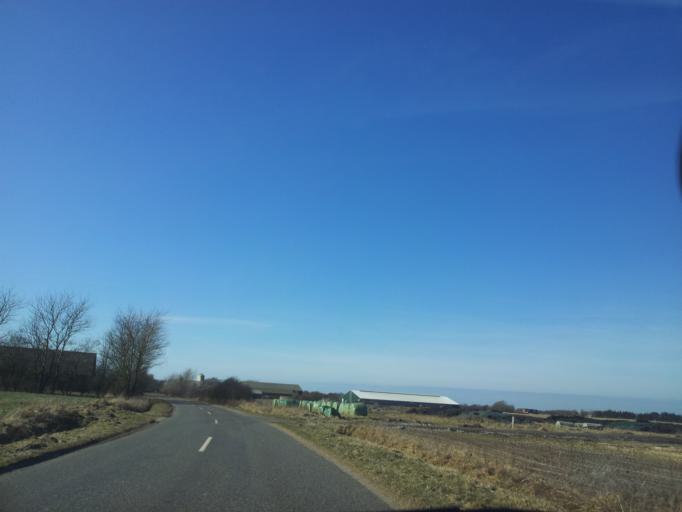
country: DK
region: South Denmark
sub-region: Tonder Kommune
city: Sherrebek
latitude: 55.1729
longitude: 8.7281
